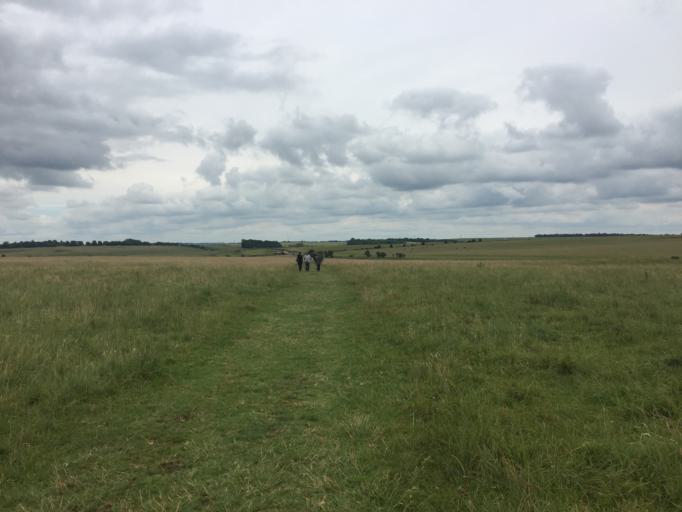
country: GB
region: England
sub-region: Wiltshire
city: Durnford
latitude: 51.1838
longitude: -1.8378
